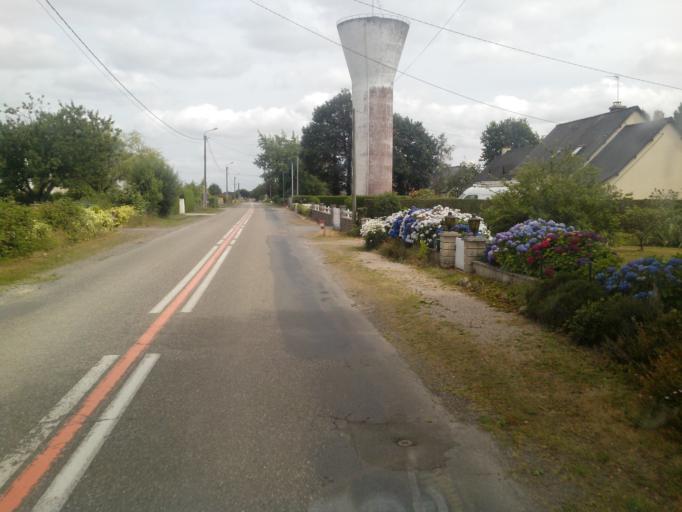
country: FR
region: Brittany
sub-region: Departement d'Ille-et-Vilaine
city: Plelan-le-Grand
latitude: 47.9992
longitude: -2.0896
